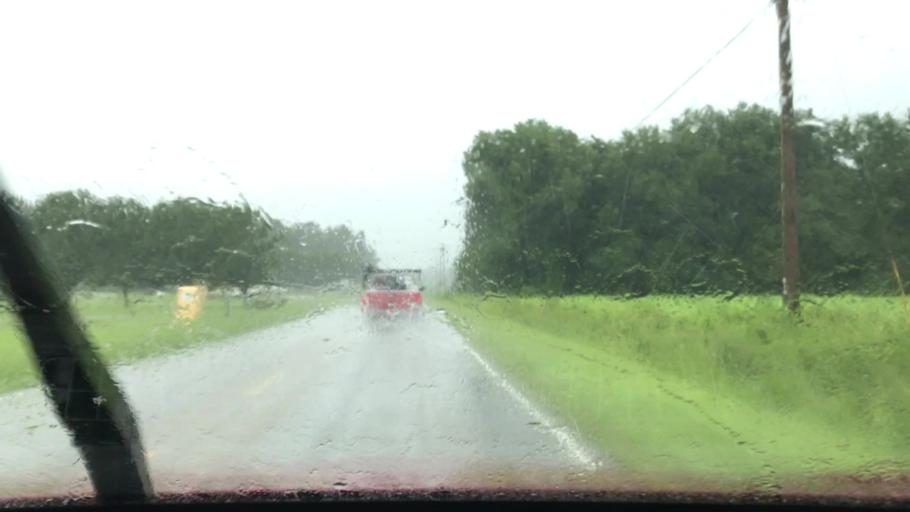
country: US
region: South Carolina
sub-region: Horry County
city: Red Hill
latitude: 33.8613
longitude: -78.9947
